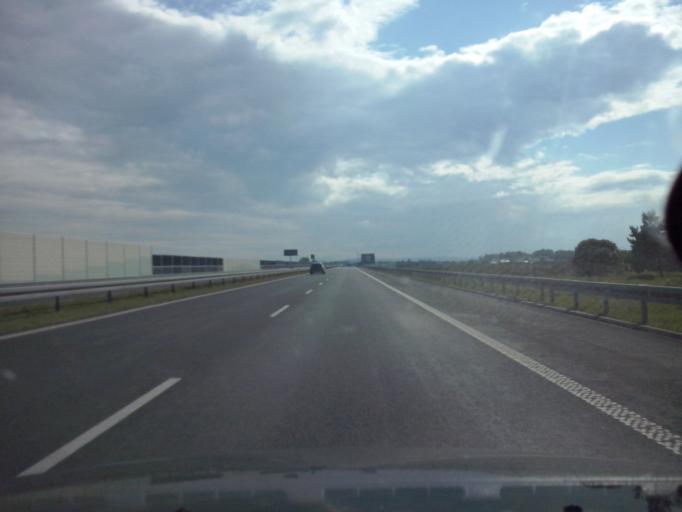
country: PL
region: Lesser Poland Voivodeship
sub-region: Powiat tarnowski
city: Wierzchoslawice
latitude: 50.0243
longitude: 20.8754
